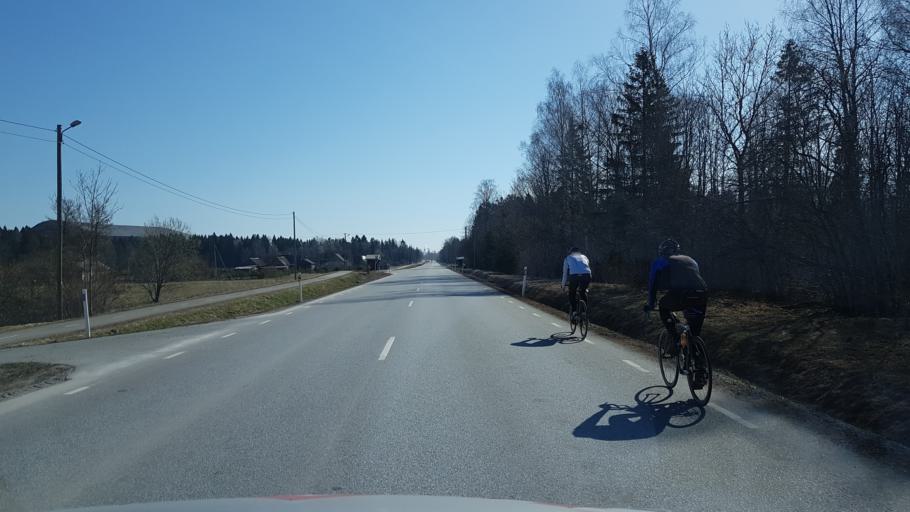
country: EE
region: Ida-Virumaa
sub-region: Kivioli linn
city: Kivioli
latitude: 59.3557
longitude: 26.9053
